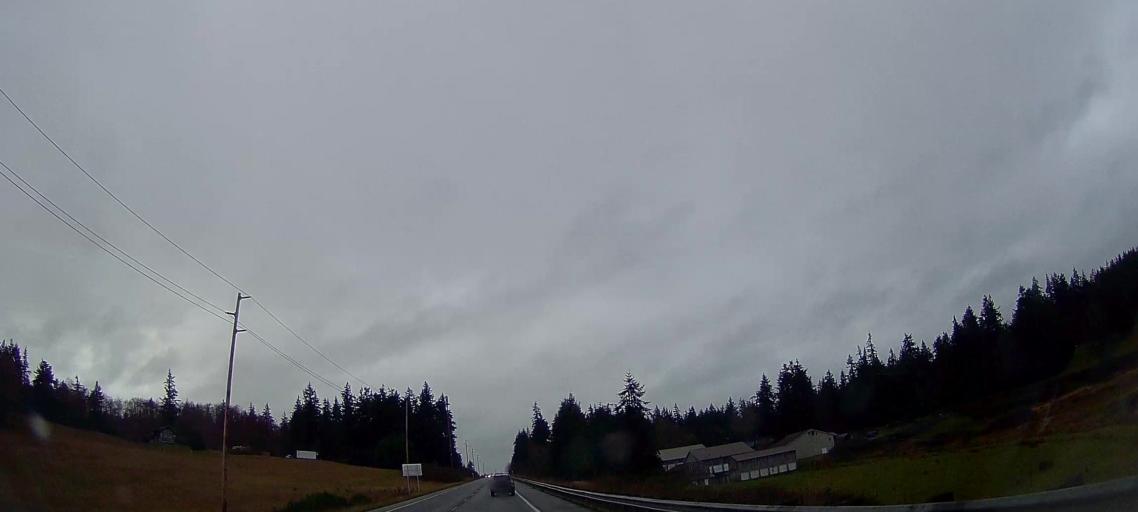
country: US
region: Washington
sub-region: Island County
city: Freeland
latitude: 48.0070
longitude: -122.4916
